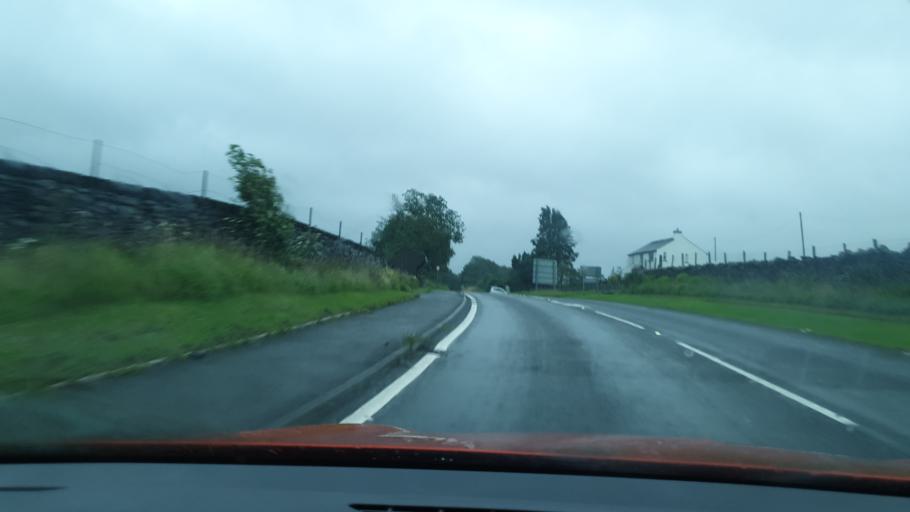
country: GB
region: England
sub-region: Cumbria
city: Ulverston
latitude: 54.2576
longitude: -3.0781
